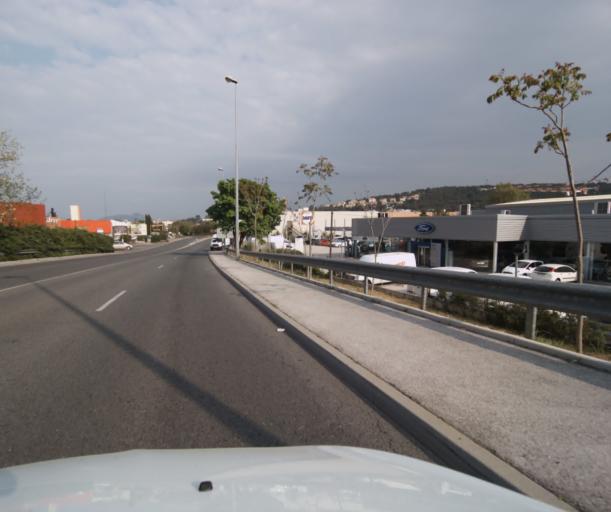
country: FR
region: Provence-Alpes-Cote d'Azur
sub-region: Departement du Var
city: La Valette-du-Var
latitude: 43.1372
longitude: 5.9978
